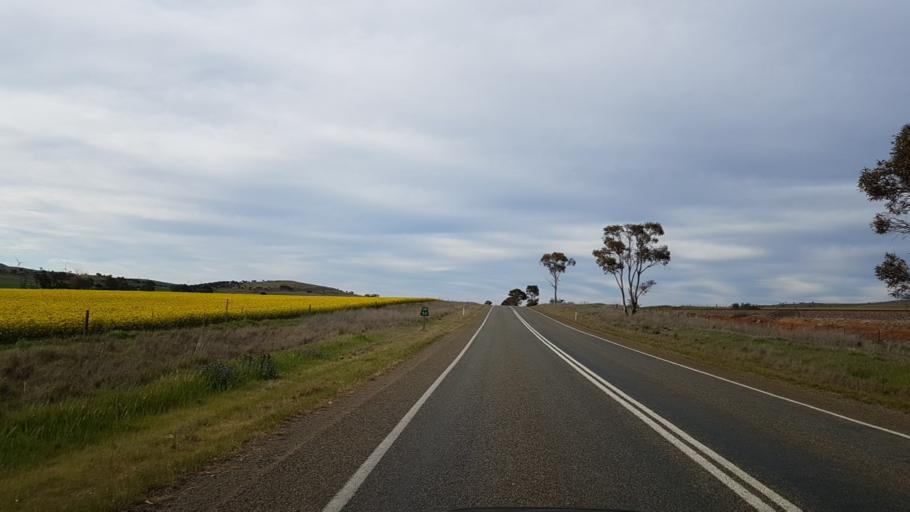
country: AU
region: South Australia
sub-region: Northern Areas
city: Jamestown
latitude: -33.1477
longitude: 138.6155
